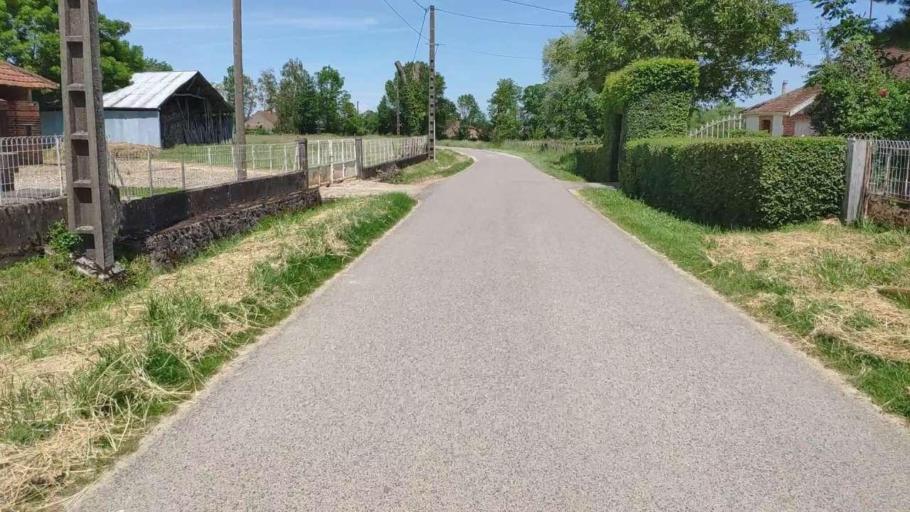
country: FR
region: Franche-Comte
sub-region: Departement du Jura
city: Bletterans
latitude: 46.7928
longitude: 5.3771
